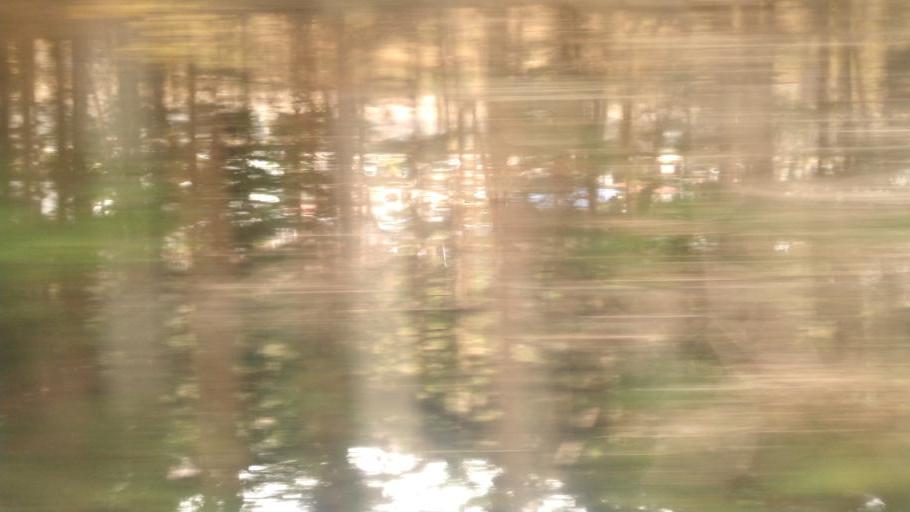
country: JP
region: Nagano
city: Tatsuno
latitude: 35.9751
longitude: 137.8240
